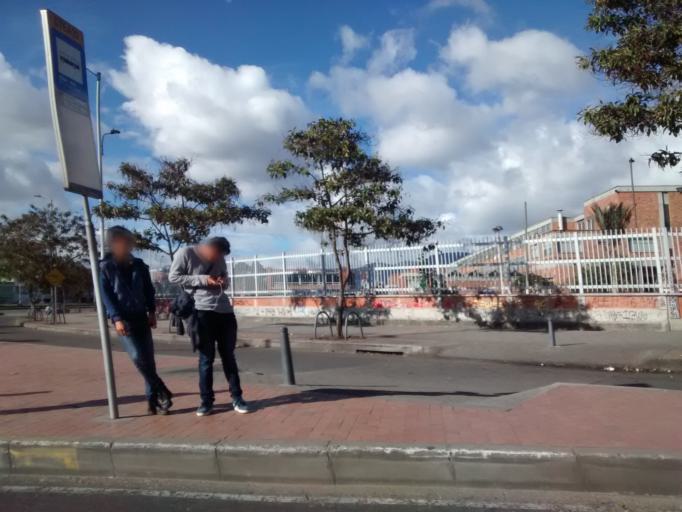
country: CO
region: Bogota D.C.
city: Bogota
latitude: 4.5955
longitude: -74.1130
